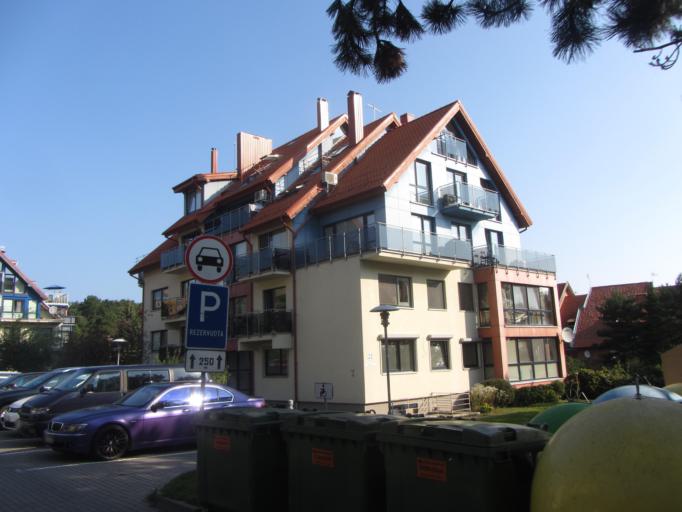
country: LT
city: Nida
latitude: 55.3028
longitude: 21.0011
